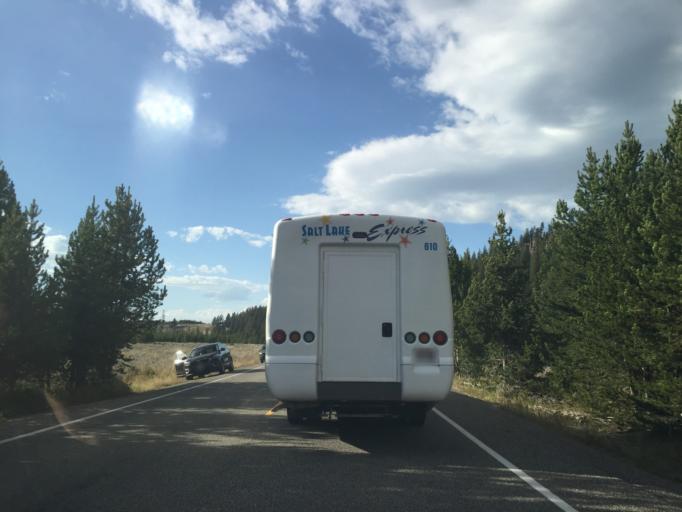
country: US
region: Montana
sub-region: Gallatin County
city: West Yellowstone
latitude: 44.6660
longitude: -110.9692
